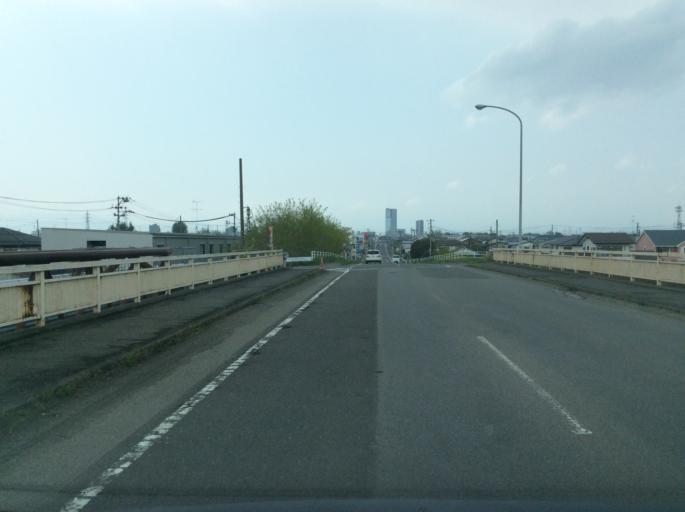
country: JP
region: Fukushima
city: Koriyama
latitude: 37.3824
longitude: 140.4057
